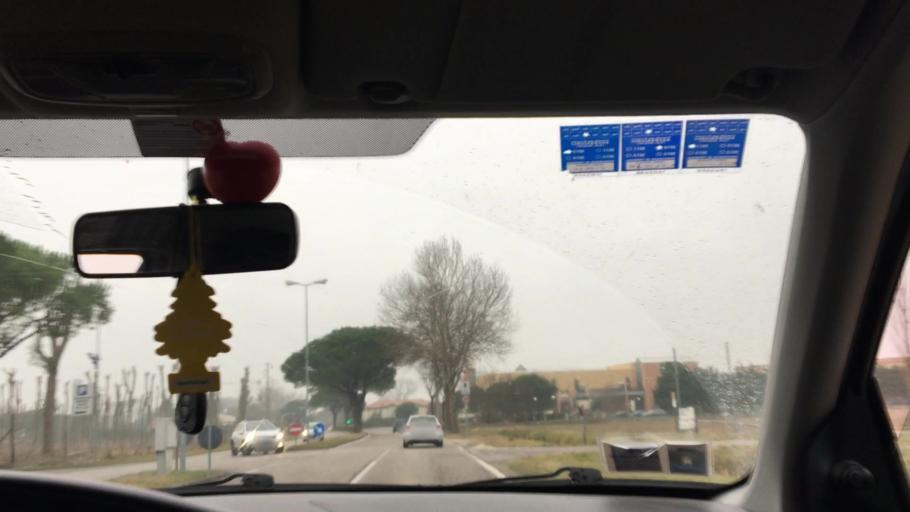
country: IT
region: Veneto
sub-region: Provincia di Venezia
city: Lido di Iesolo
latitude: 45.5122
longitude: 12.6506
